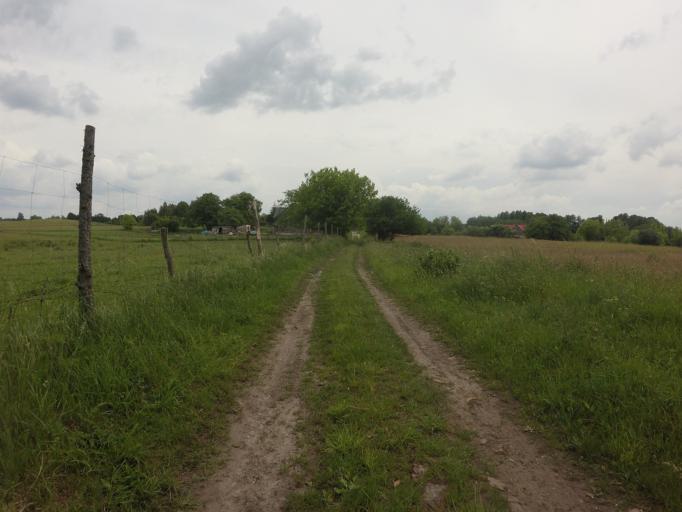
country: PL
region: West Pomeranian Voivodeship
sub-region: Powiat stargardzki
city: Dobrzany
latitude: 53.3234
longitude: 15.4763
